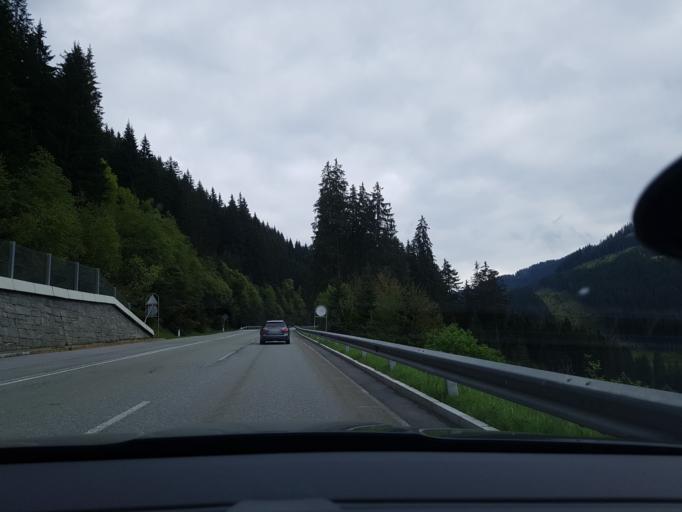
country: AT
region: Tyrol
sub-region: Politischer Bezirk Kitzbuhel
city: Jochberg
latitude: 47.3287
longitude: 12.4096
